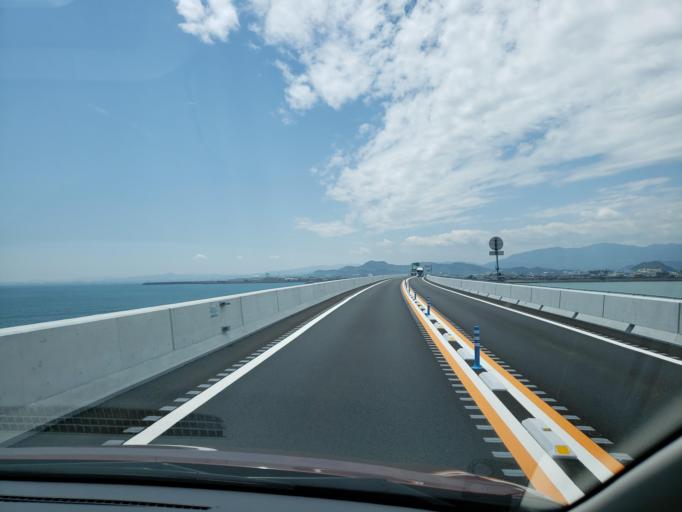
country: JP
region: Tokushima
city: Tokushima-shi
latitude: 34.0808
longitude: 134.6012
